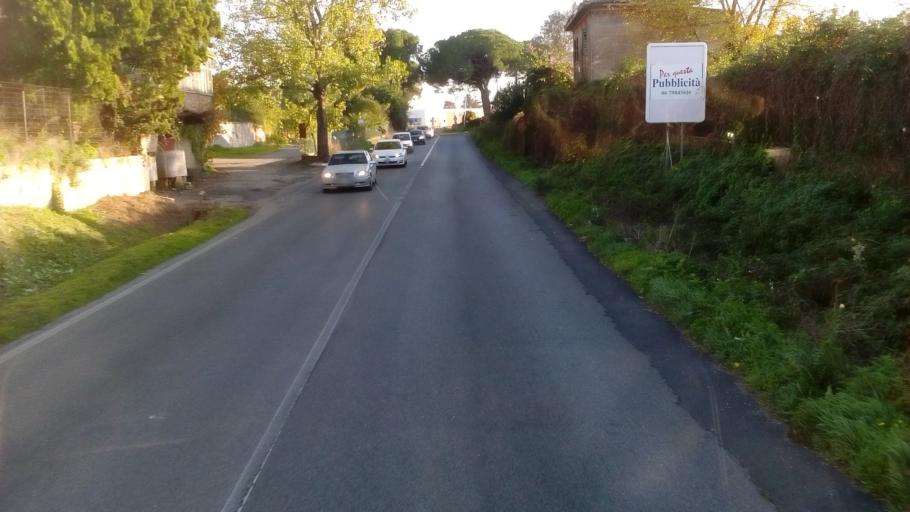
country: IT
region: Latium
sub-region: Citta metropolitana di Roma Capitale
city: Pavona
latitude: 41.7202
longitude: 12.6216
